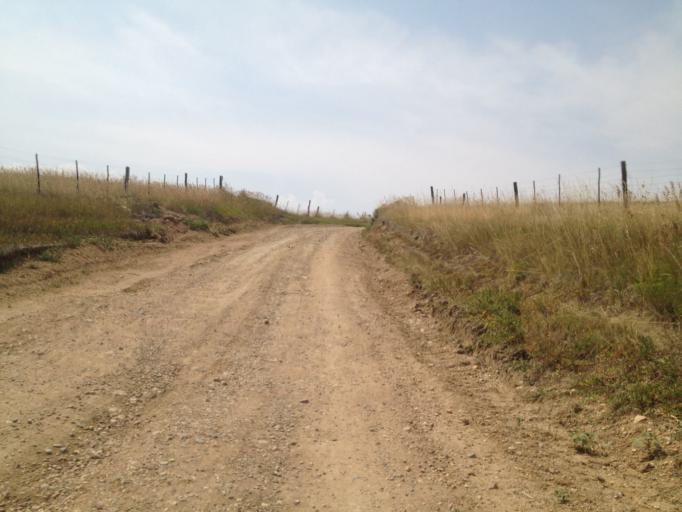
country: US
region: Colorado
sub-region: Boulder County
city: Superior
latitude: 39.9393
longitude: -105.1972
